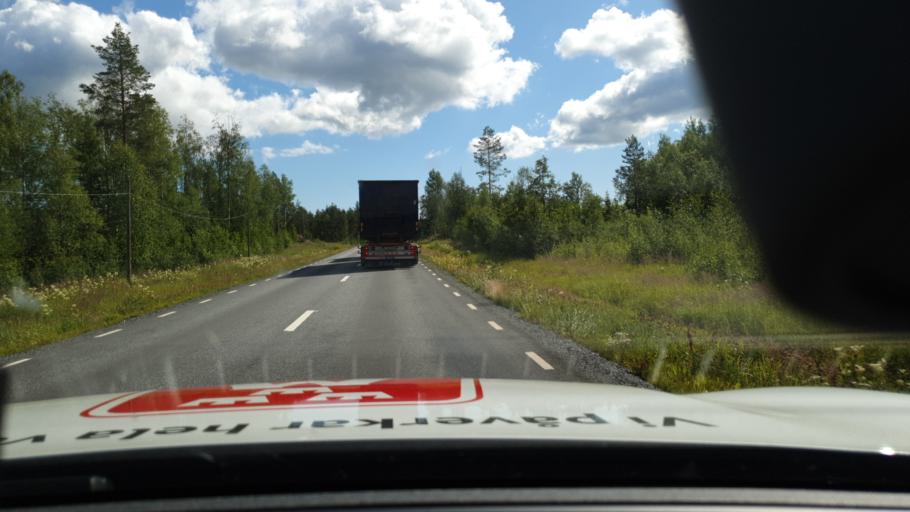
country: SE
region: Norrbotten
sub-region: Lulea Kommun
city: Ranea
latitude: 65.7902
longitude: 22.1390
